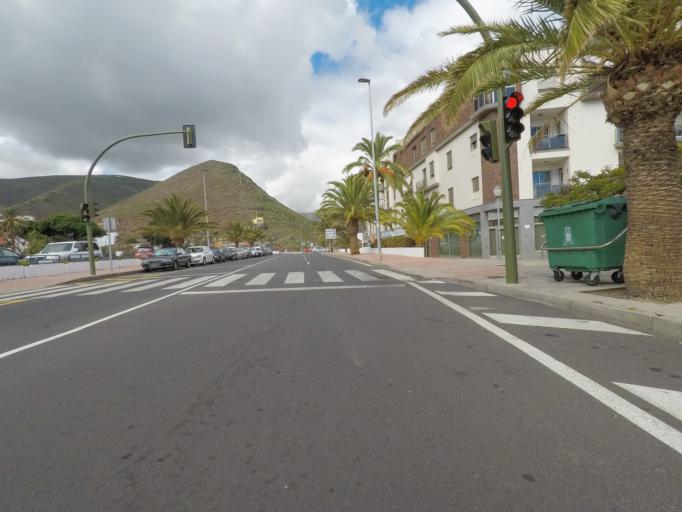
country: ES
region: Canary Islands
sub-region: Provincia de Santa Cruz de Tenerife
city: San Sebastian de la Gomera
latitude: 28.0907
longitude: -17.1129
